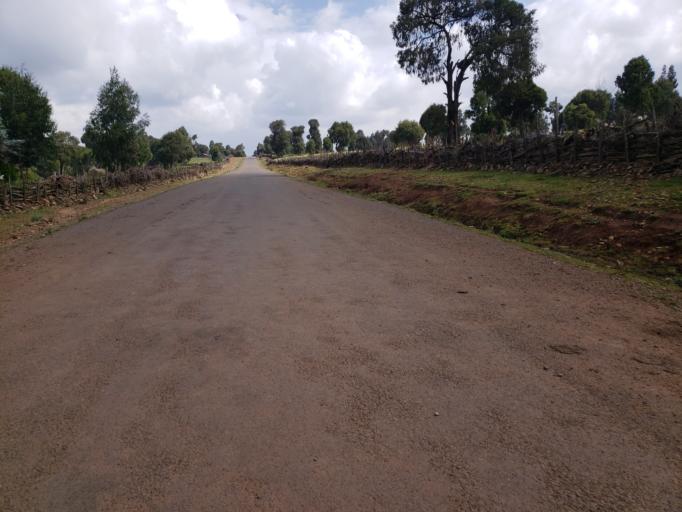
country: ET
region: Oromiya
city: Dodola
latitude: 6.8715
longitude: 39.3872
